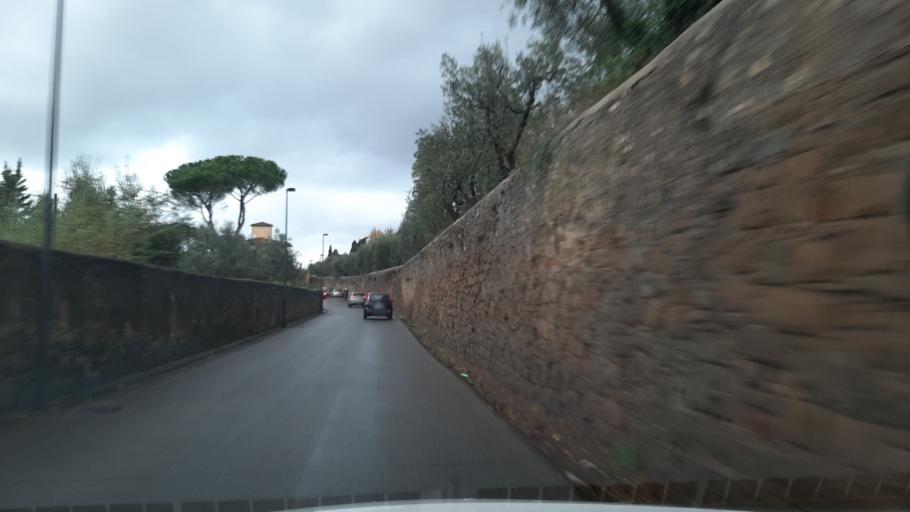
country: IT
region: Tuscany
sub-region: Province of Florence
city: Florence
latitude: 43.8092
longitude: 11.2595
